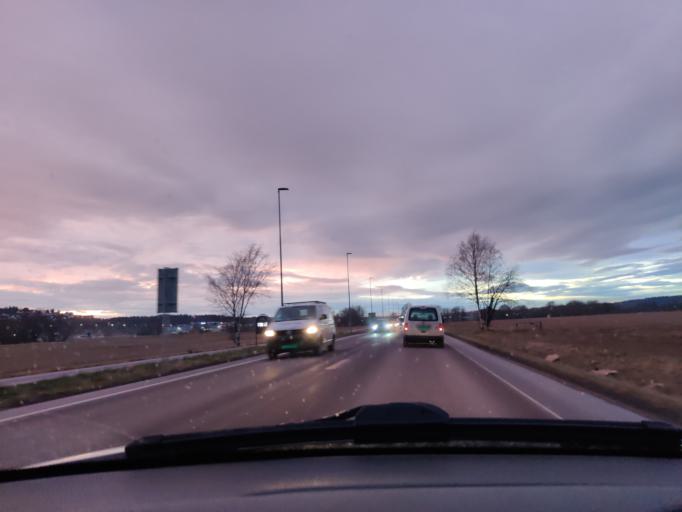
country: NO
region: Vestfold
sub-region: Tonsberg
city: Tonsberg
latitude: 59.2820
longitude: 10.3782
